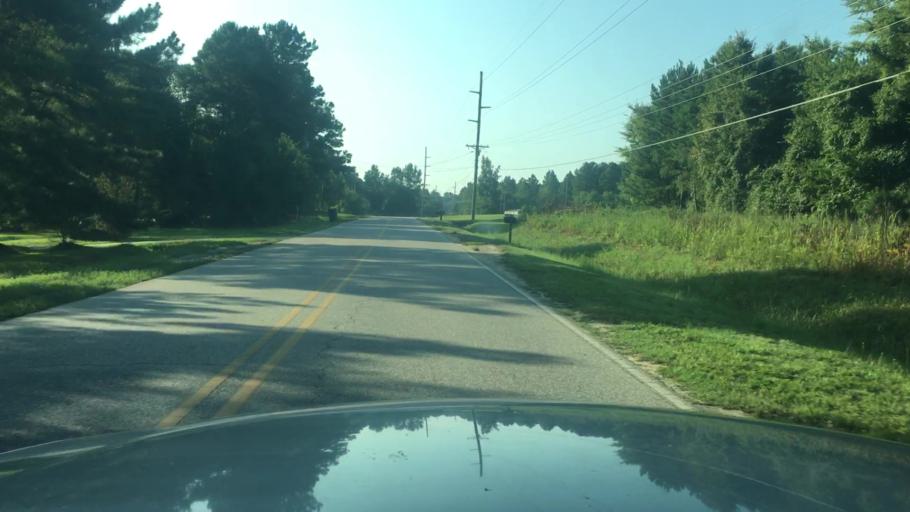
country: US
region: North Carolina
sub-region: Cumberland County
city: Spring Lake
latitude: 35.2096
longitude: -78.8946
